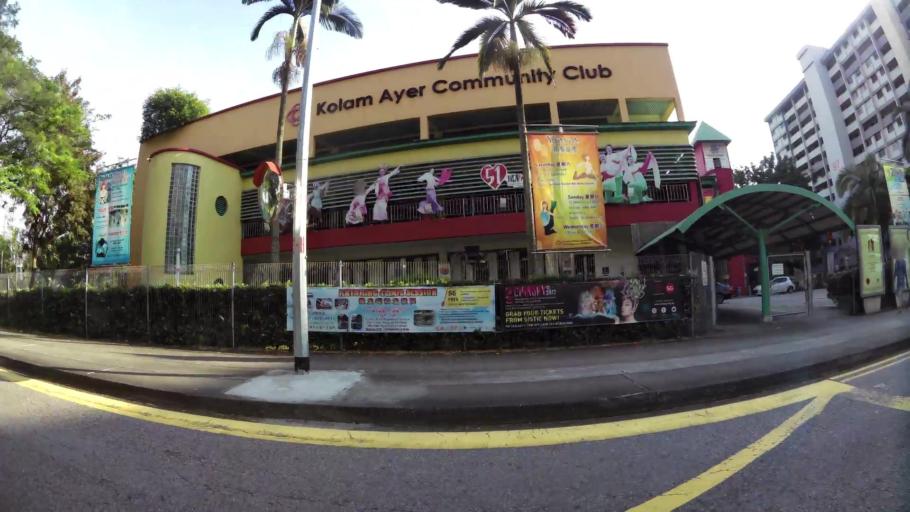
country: SG
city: Singapore
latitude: 1.3239
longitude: 103.8696
